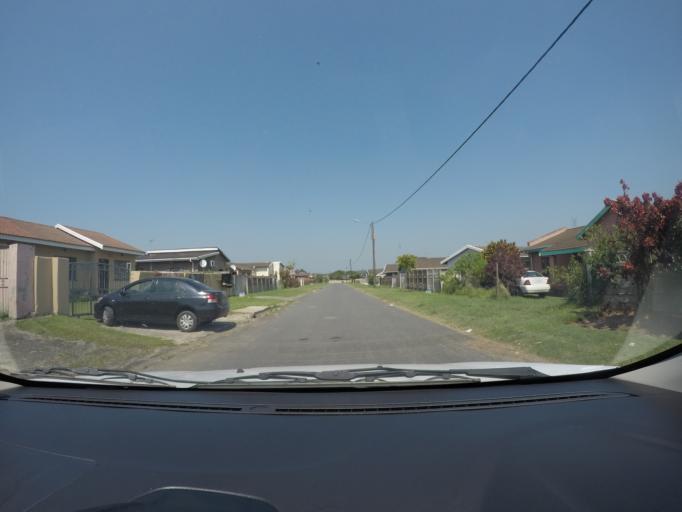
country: ZA
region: KwaZulu-Natal
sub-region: uThungulu District Municipality
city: eSikhawini
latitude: -28.8676
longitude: 31.9167
